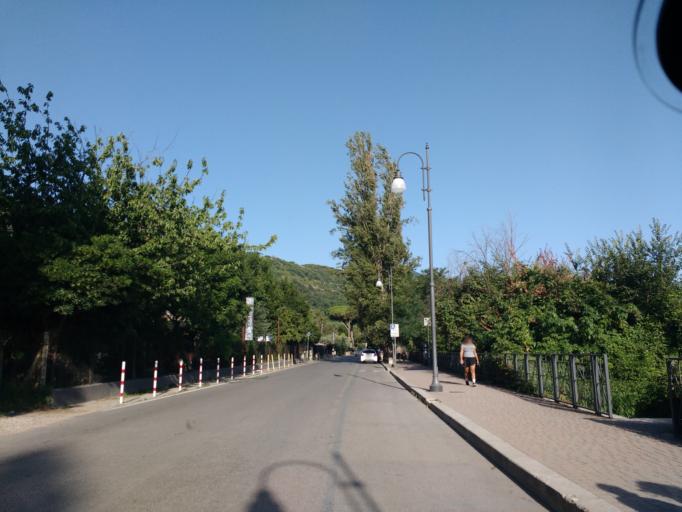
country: IT
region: Latium
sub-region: Citta metropolitana di Roma Capitale
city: Castel Gandolfo
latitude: 41.7613
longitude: 12.6611
